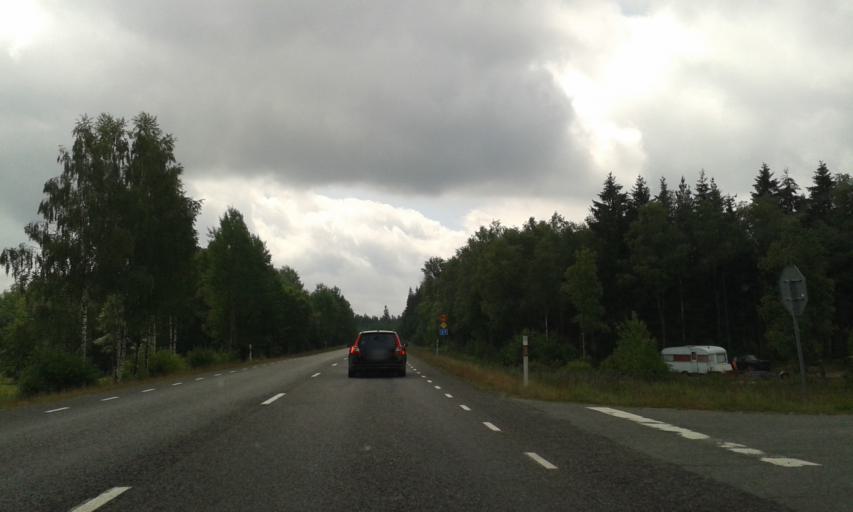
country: SE
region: Vaestra Goetaland
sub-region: Tranemo Kommun
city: Tranemo
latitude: 57.4312
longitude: 13.4467
